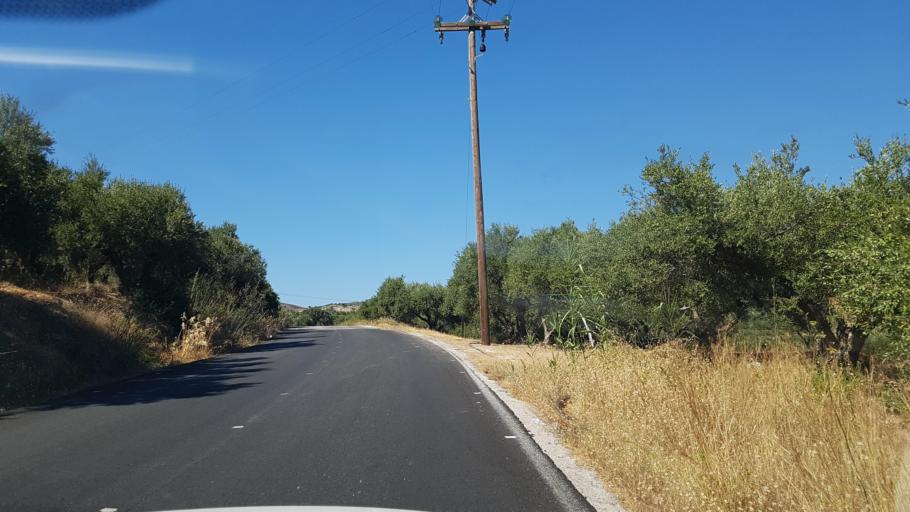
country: GR
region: Crete
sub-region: Nomos Chanias
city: Kissamos
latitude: 35.4994
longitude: 23.7226
